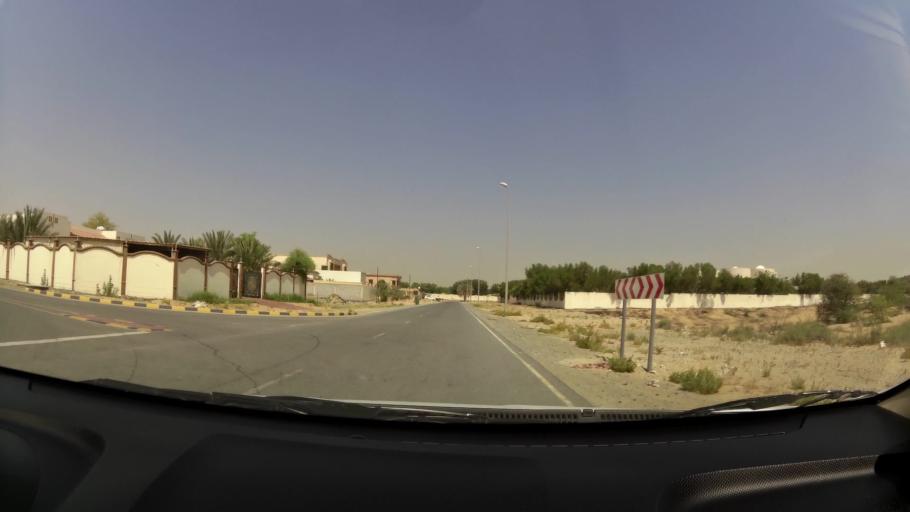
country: AE
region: Ajman
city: Ajman
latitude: 25.3975
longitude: 55.5395
